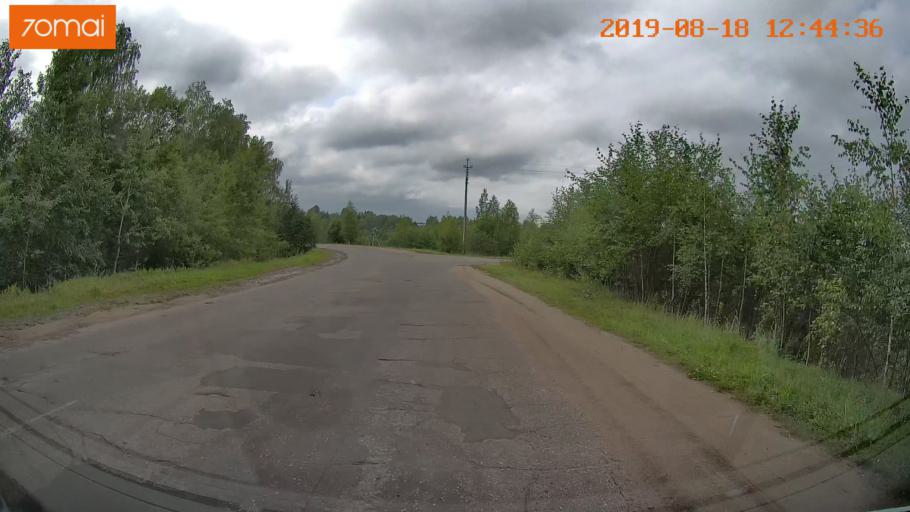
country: RU
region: Ivanovo
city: Novo-Talitsy
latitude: 57.0473
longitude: 40.8514
